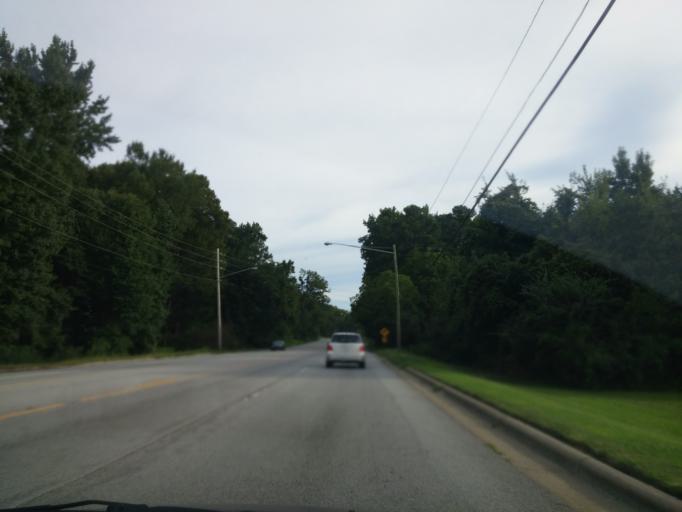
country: US
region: North Carolina
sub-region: Pitt County
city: Summerfield
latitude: 35.5858
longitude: -77.3962
